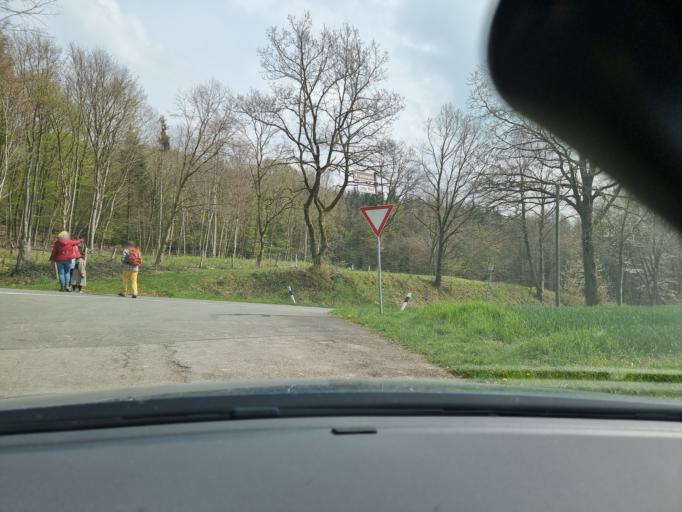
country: DE
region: North Rhine-Westphalia
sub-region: Regierungsbezirk Detmold
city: Dorentrup
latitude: 52.1271
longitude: 9.0140
